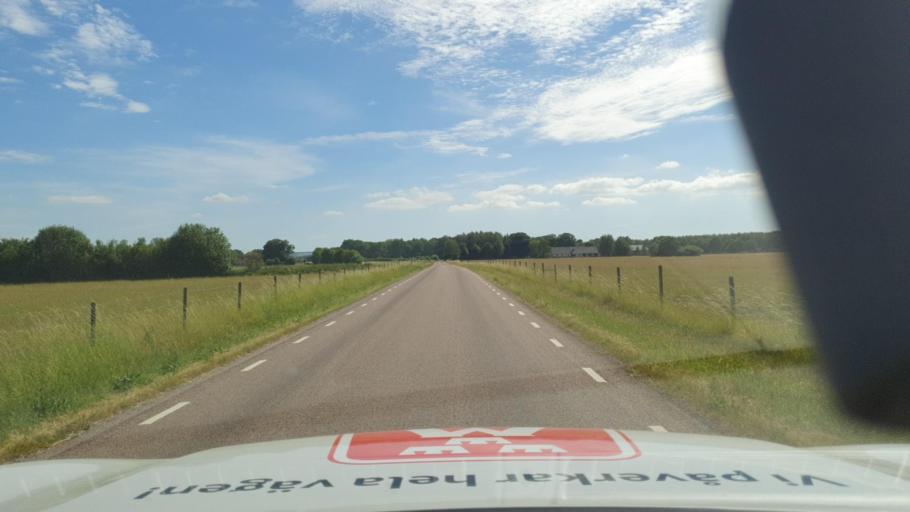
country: SE
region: Skane
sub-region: Sjobo Kommun
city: Blentarp
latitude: 55.6181
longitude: 13.6220
